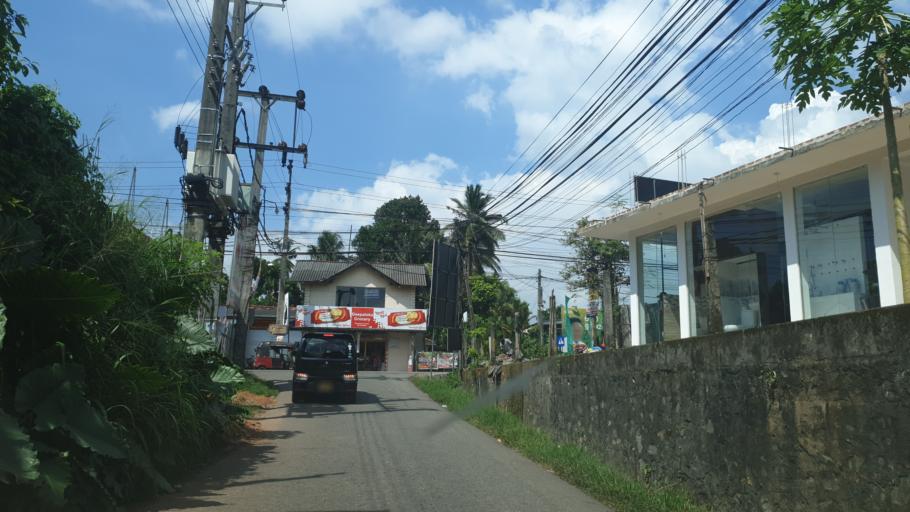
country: LK
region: Western
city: Panadura
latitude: 6.7100
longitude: 79.9824
